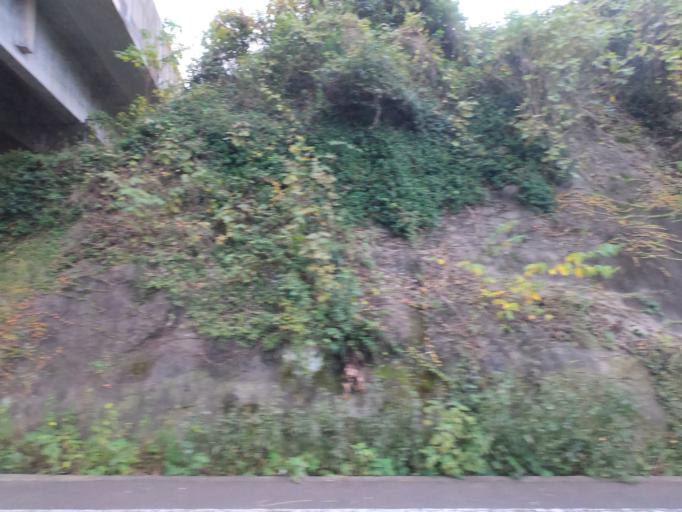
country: JP
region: Kumamoto
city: Minamata
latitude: 32.2618
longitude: 130.5084
